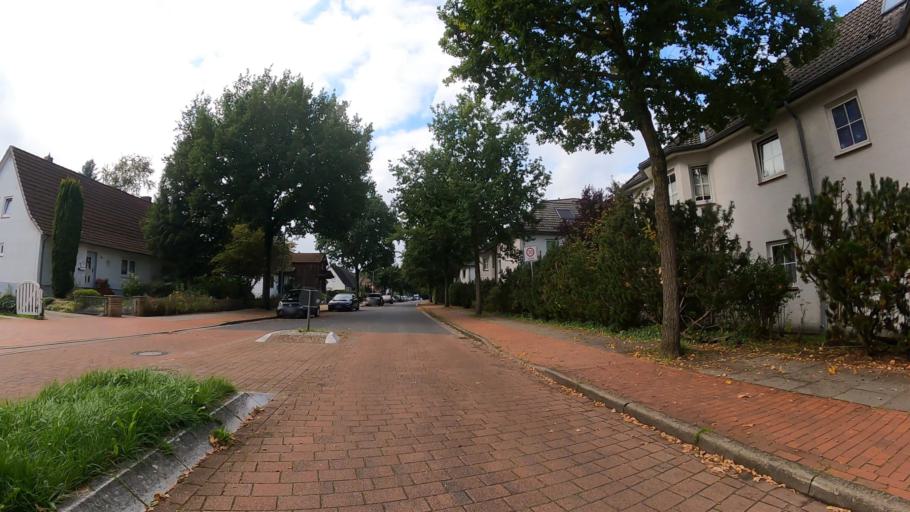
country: DE
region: Schleswig-Holstein
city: Klein Nordende
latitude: 53.7330
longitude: 9.6773
